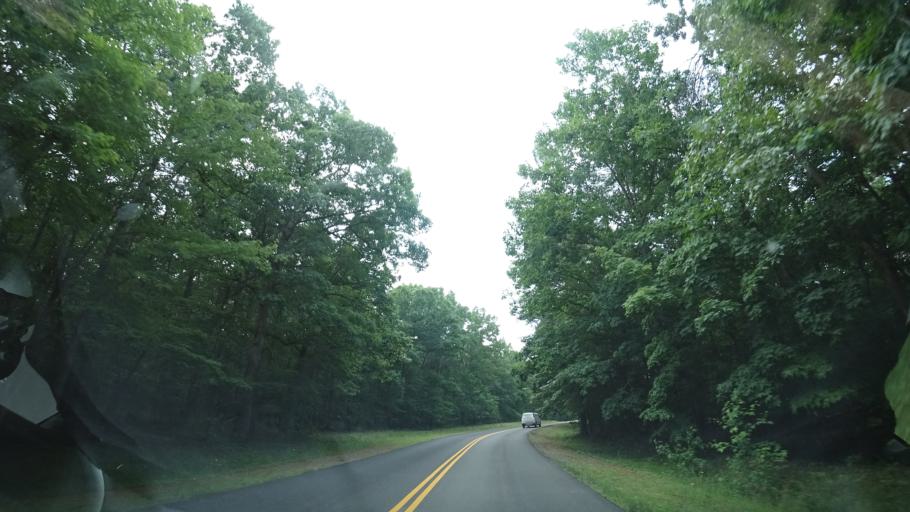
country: US
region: Virginia
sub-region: Louisa County
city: Louisa
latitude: 38.1379
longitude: -77.8180
